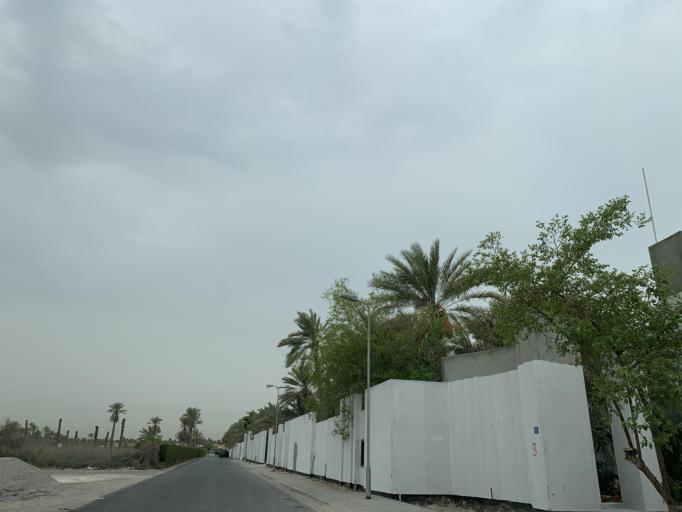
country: BH
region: Northern
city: Madinat `Isa
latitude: 26.1914
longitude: 50.4702
